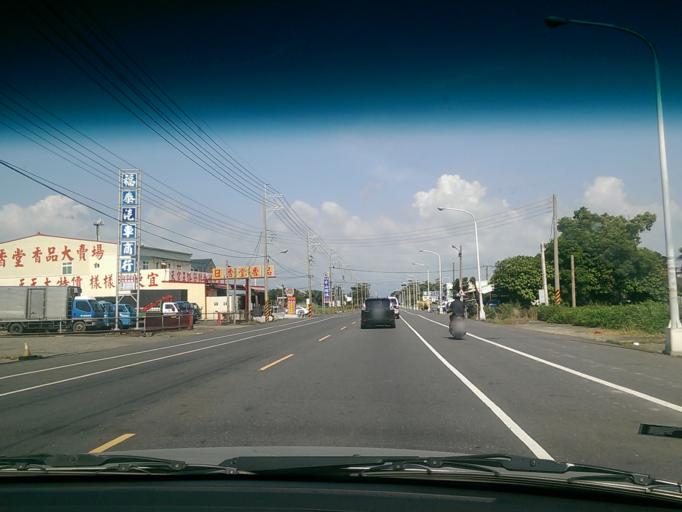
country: TW
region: Taiwan
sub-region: Chiayi
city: Taibao
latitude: 23.5609
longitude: 120.3166
